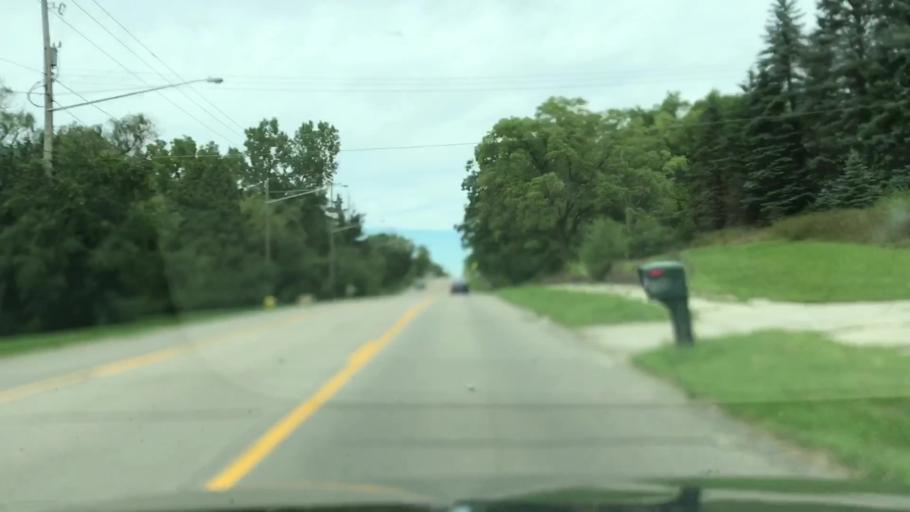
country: US
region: Michigan
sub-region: Kent County
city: East Grand Rapids
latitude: 42.9889
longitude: -85.6006
